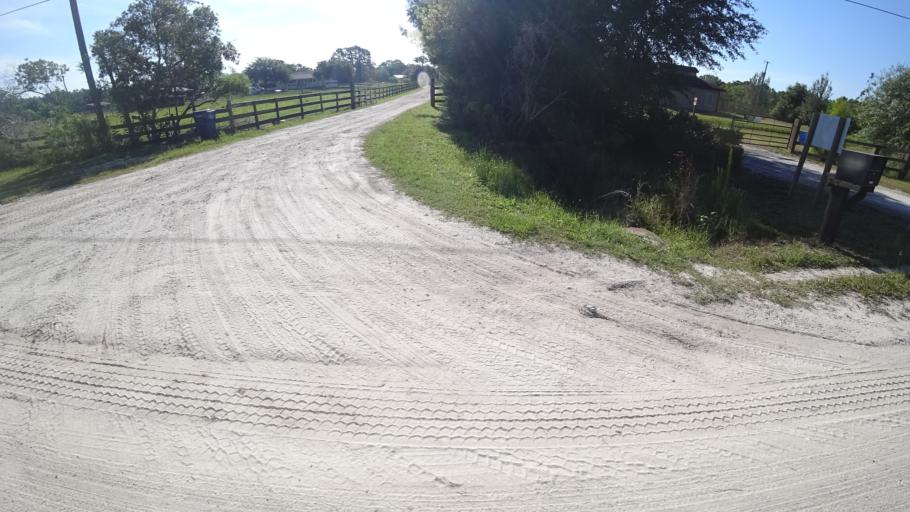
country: US
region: Florida
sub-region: Sarasota County
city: Fruitville
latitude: 27.4168
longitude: -82.2519
